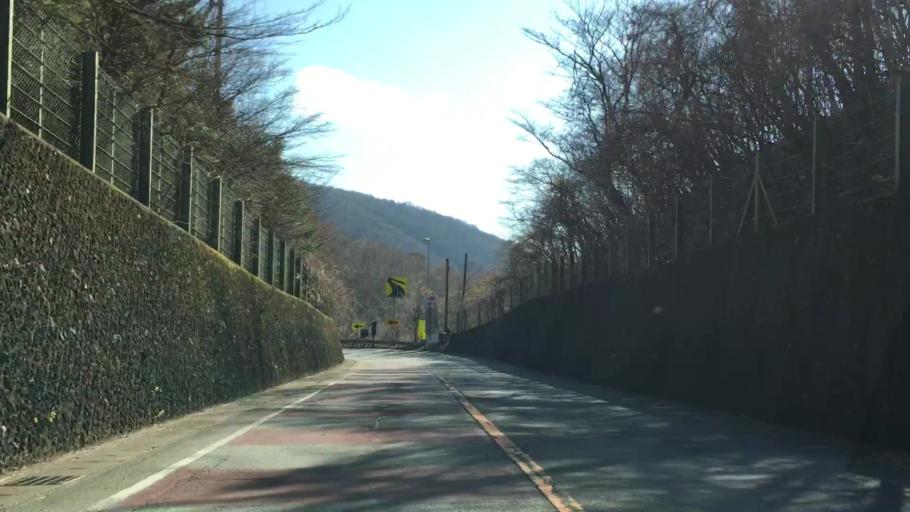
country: JP
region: Shizuoka
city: Gotemba
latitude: 35.3926
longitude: 138.8641
